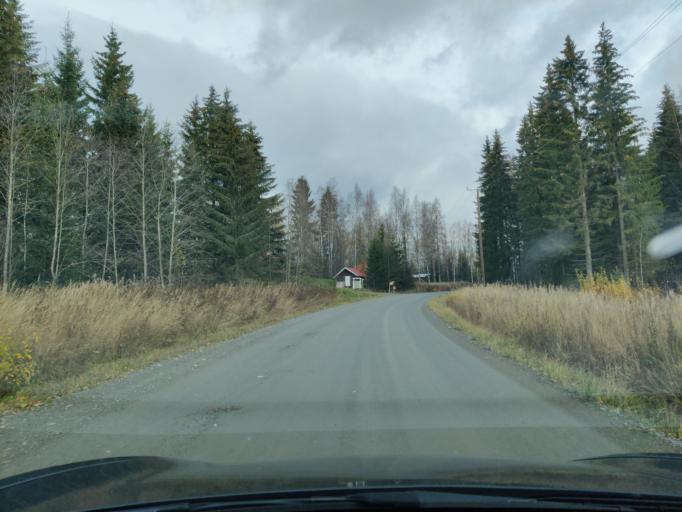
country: FI
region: Northern Savo
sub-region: Kuopio
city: Siilinjaervi
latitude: 63.1168
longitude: 27.5445
